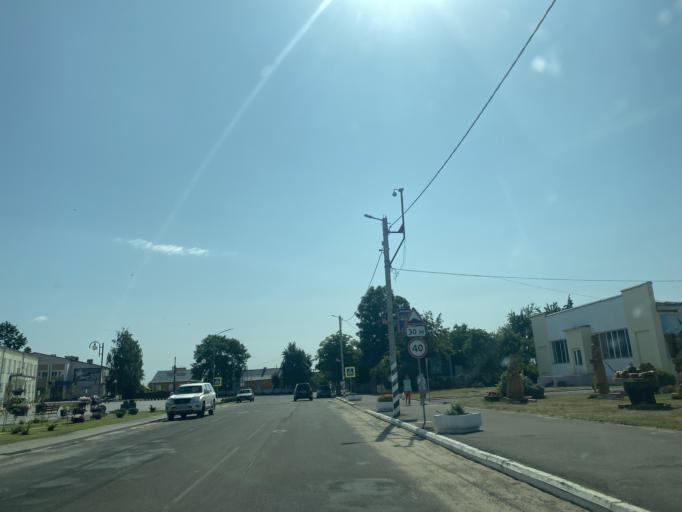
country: BY
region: Brest
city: Ivanava
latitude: 52.3166
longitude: 25.6088
